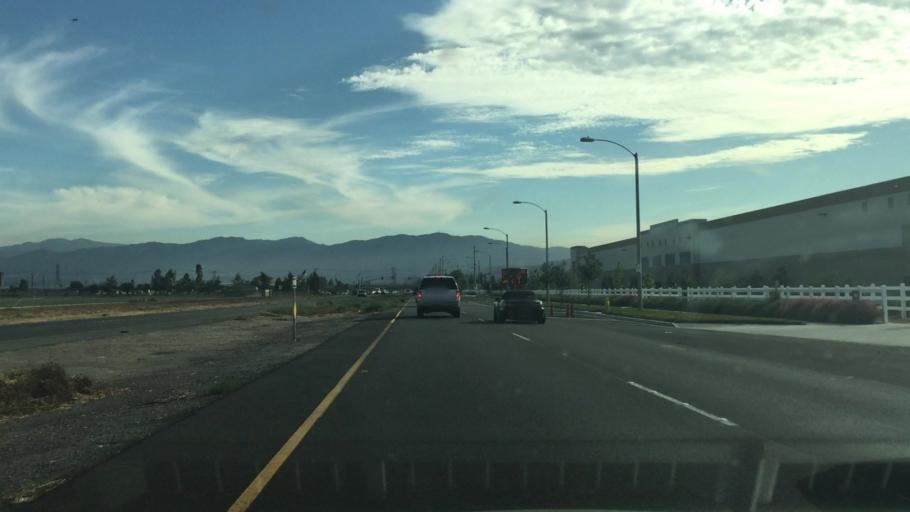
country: US
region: California
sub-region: San Bernardino County
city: Chino
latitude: 33.9723
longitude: -117.6508
